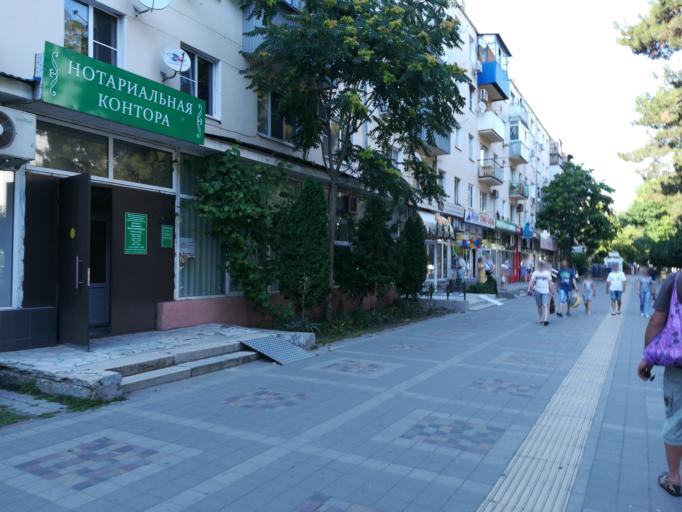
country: RU
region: Krasnodarskiy
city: Anapa
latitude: 44.8994
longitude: 37.3284
